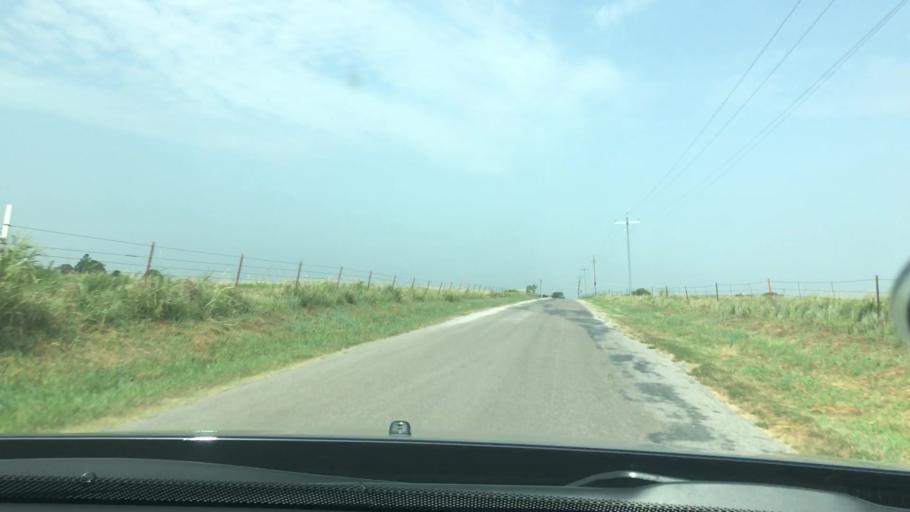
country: US
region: Oklahoma
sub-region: Garvin County
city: Pauls Valley
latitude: 34.7967
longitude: -97.1734
